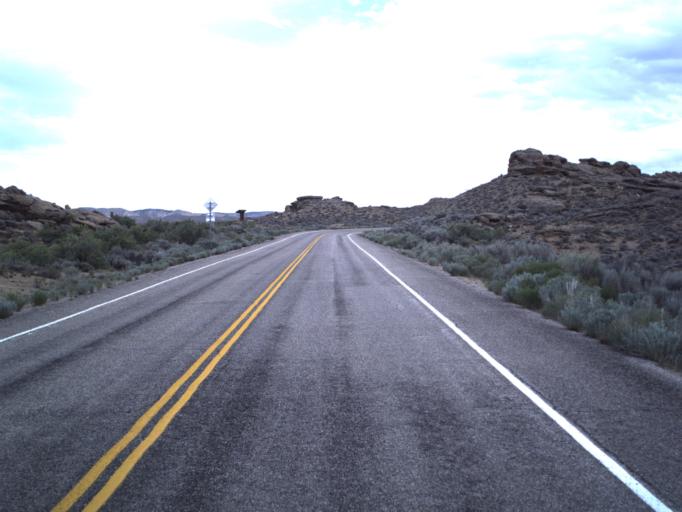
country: US
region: Colorado
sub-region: Rio Blanco County
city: Rangely
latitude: 39.9698
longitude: -109.1686
